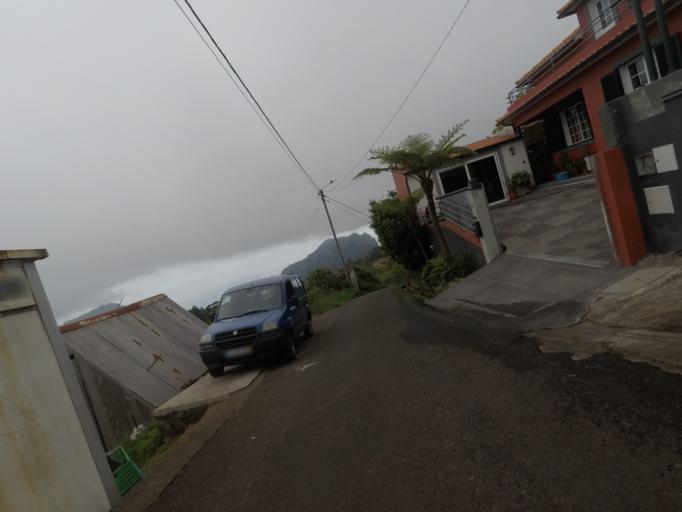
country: PT
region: Madeira
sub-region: Santana
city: Santana
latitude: 32.7516
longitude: -16.8742
